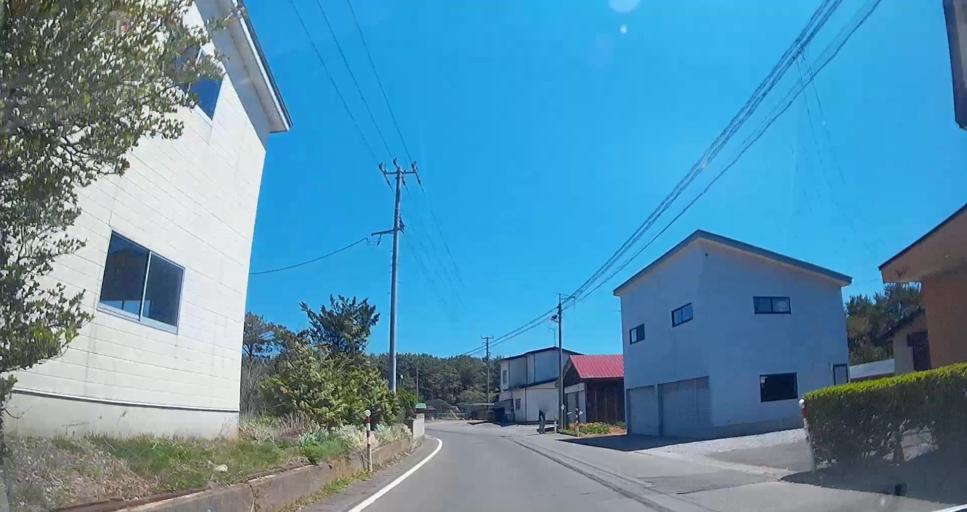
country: JP
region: Aomori
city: Mutsu
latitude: 41.2357
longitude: 141.3981
